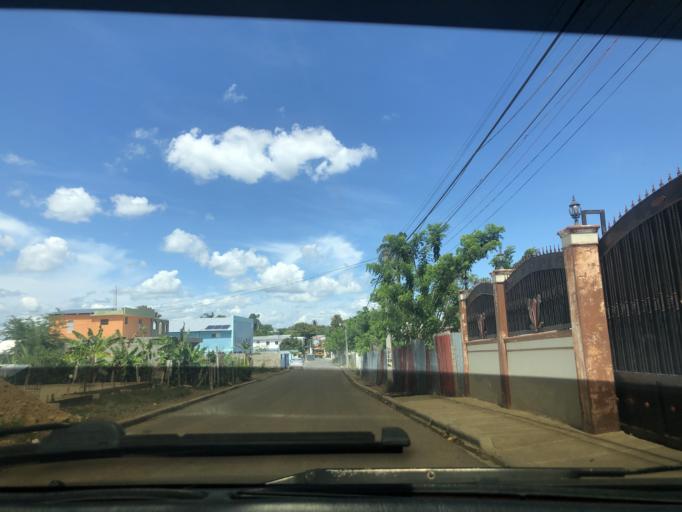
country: DO
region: Santiago
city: Santiago de los Caballeros
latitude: 19.3987
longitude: -70.6667
